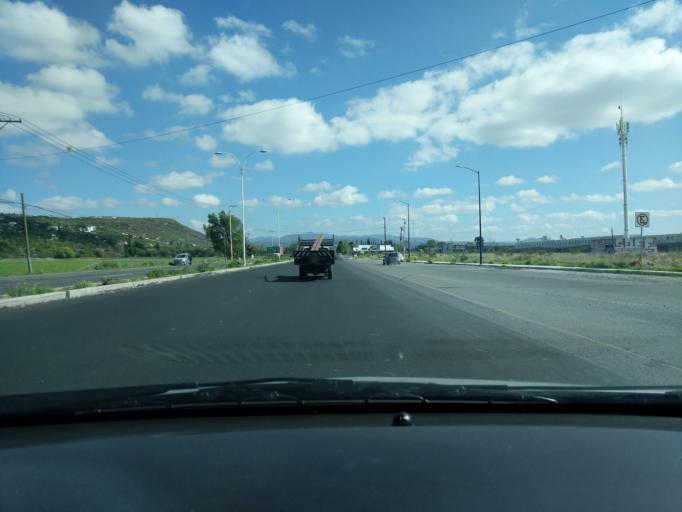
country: MX
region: Queretaro
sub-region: Queretaro
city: Patria Nueva
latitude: 20.6252
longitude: -100.4971
